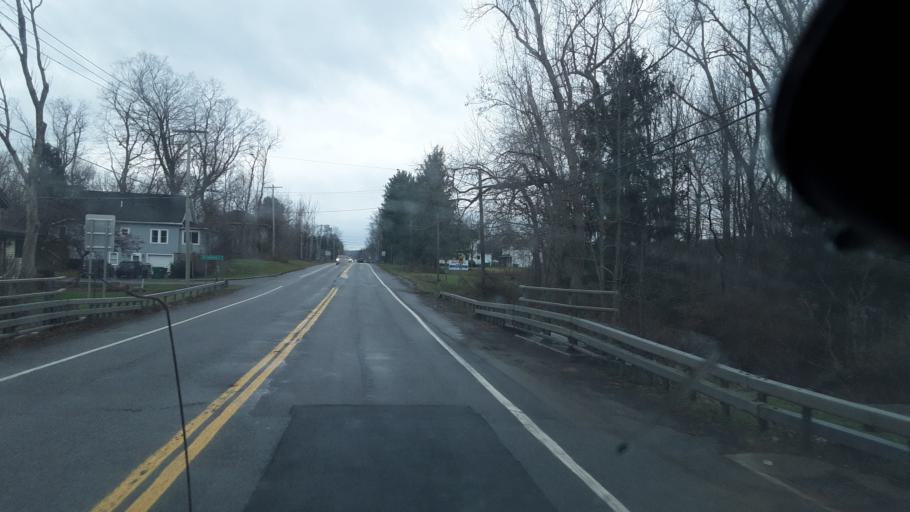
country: US
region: New York
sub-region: Erie County
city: Holland
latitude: 42.6606
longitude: -78.5550
